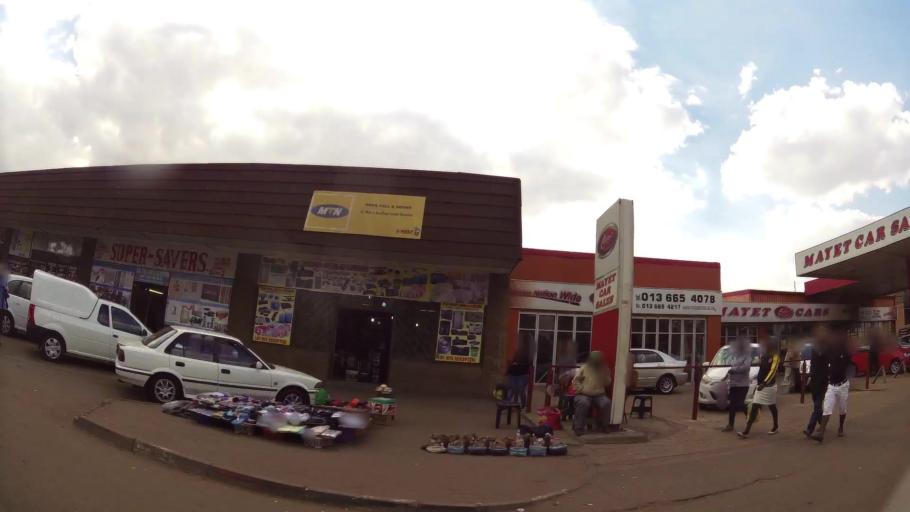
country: ZA
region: Mpumalanga
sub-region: Nkangala District Municipality
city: Delmas
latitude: -26.1516
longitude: 28.6813
